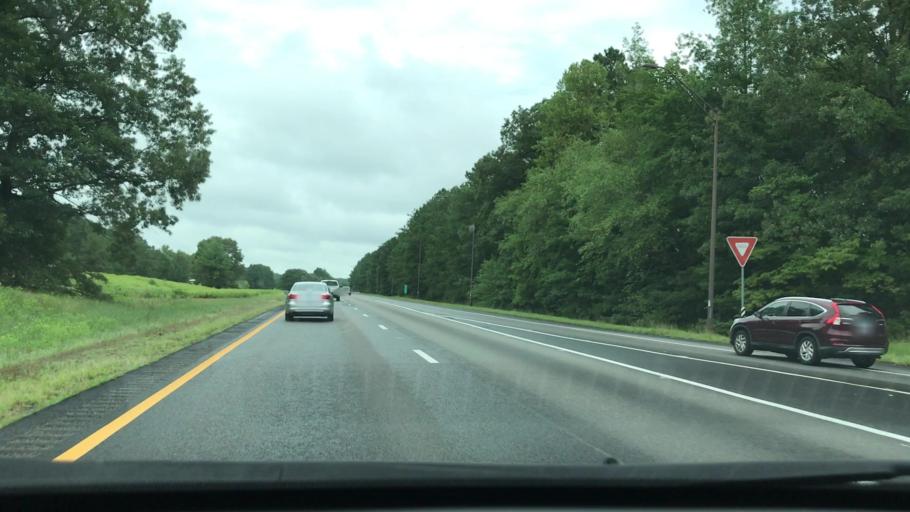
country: US
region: Virginia
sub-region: Sussex County
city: Sussex
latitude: 37.0189
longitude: -77.3918
